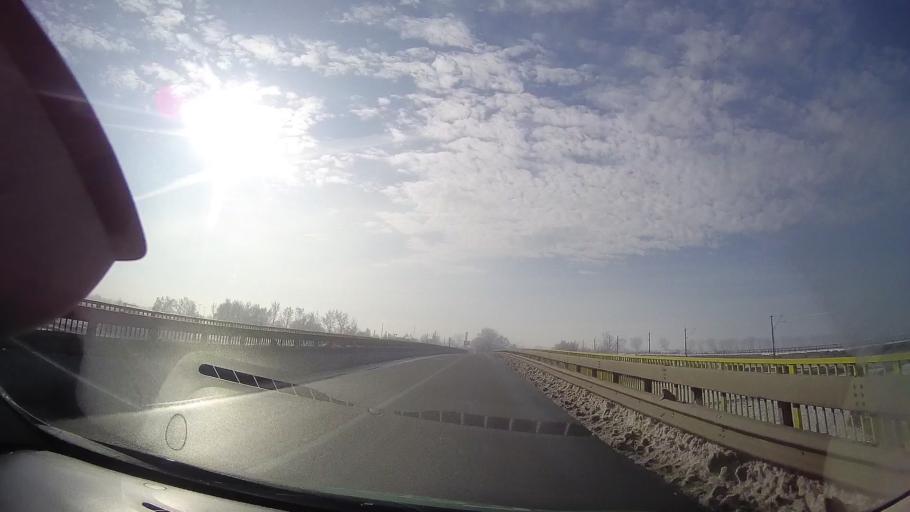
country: RO
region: Neamt
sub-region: Comuna Timisesti
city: Timisesti
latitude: 47.2467
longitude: 26.5448
